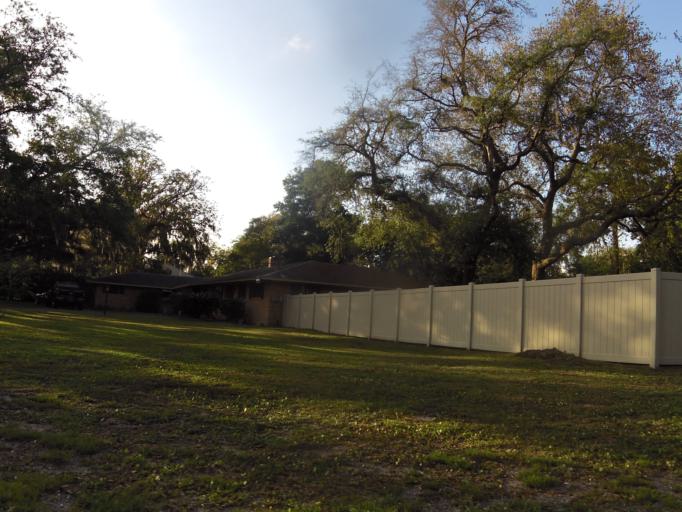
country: US
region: Florida
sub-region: Clay County
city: Orange Park
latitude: 30.2098
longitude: -81.6230
